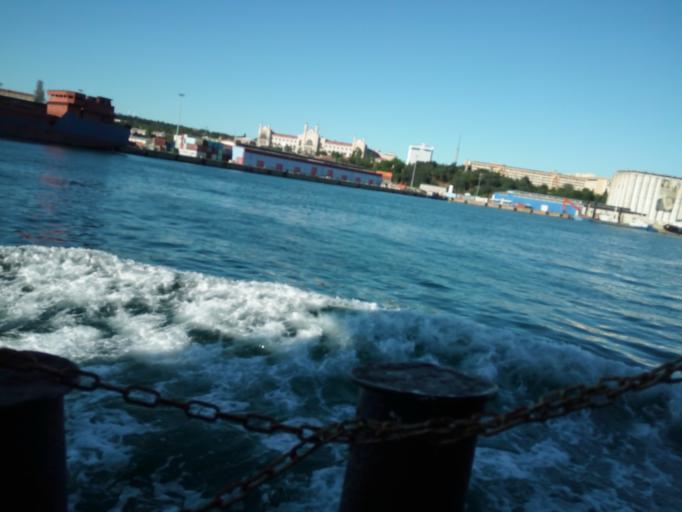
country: TR
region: Istanbul
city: UEskuedar
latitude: 40.9994
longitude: 29.0118
